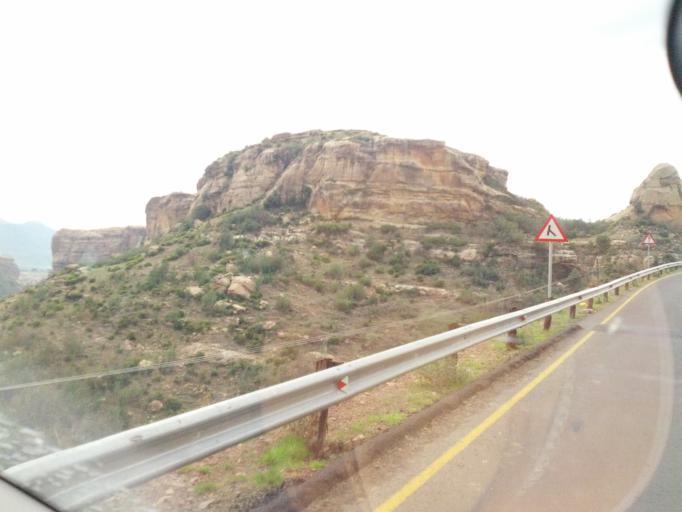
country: LS
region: Maseru
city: Nako
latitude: -29.4801
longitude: 27.7401
